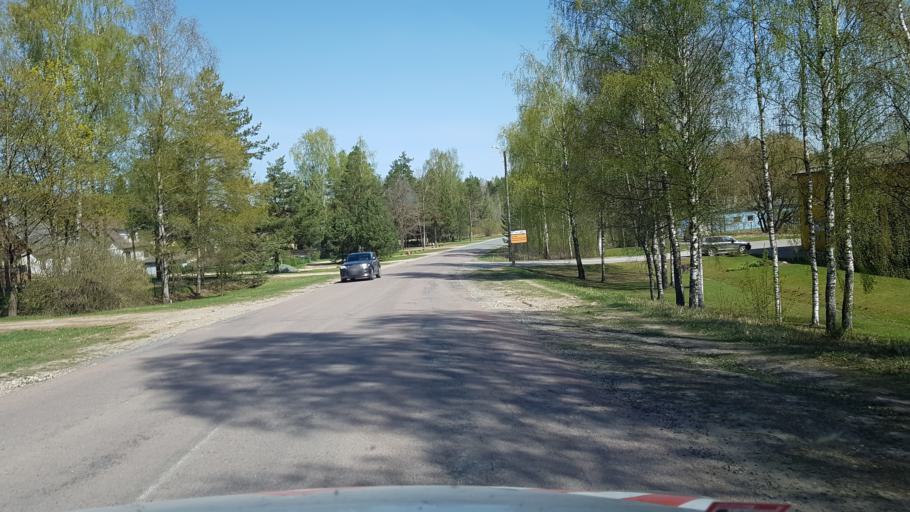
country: EE
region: Tartu
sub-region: Elva linn
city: Elva
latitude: 58.2372
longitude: 26.4125
